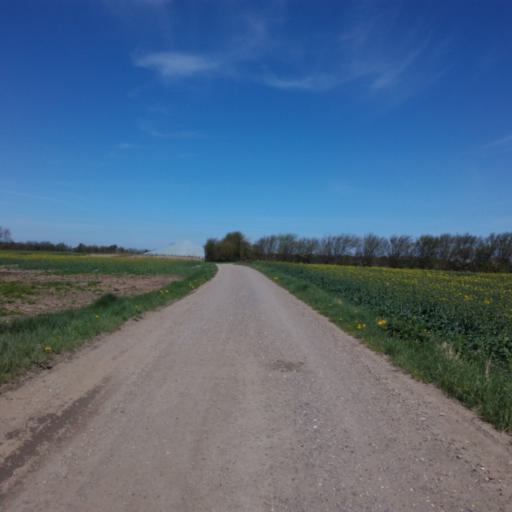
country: DK
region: South Denmark
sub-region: Vejle Kommune
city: Borkop
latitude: 55.6160
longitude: 9.6820
